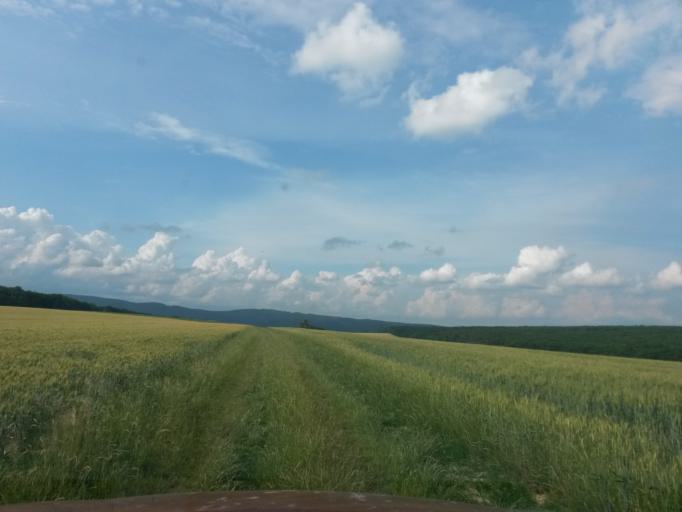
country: SK
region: Kosicky
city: Moldava nad Bodvou
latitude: 48.6304
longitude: 21.1052
